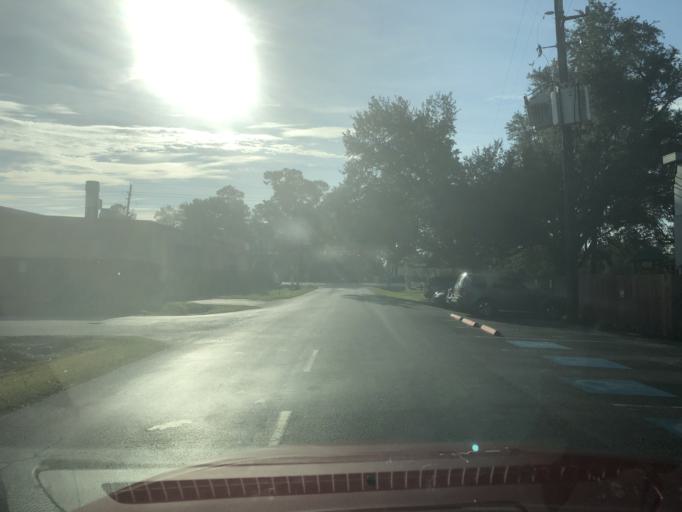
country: US
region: Texas
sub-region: Harris County
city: Spring
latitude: 30.0046
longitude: -95.4702
